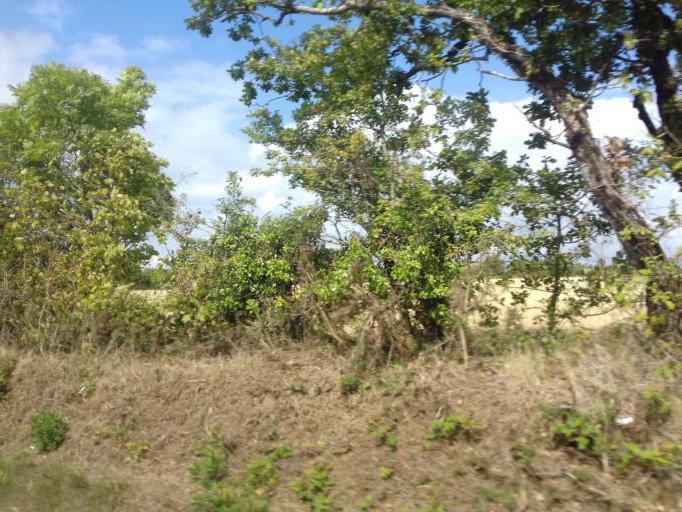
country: IE
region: Leinster
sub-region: Loch Garman
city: Loch Garman
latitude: 52.2848
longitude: -6.6379
